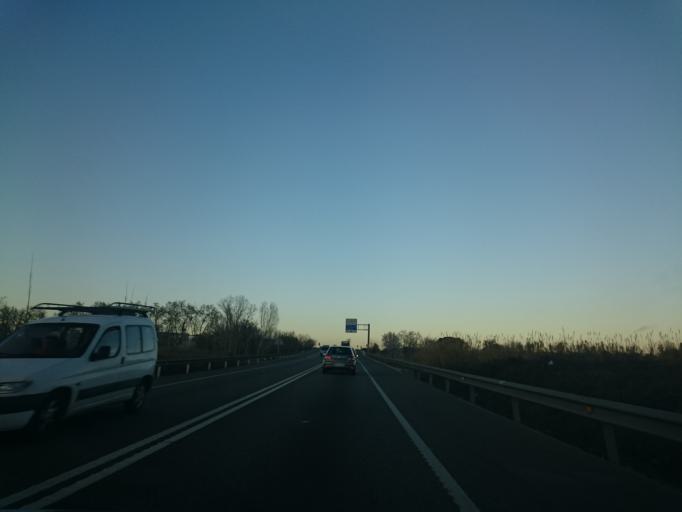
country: ES
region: Catalonia
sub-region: Provincia de Barcelona
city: Vilafranca del Penedes
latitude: 41.3443
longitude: 1.7121
